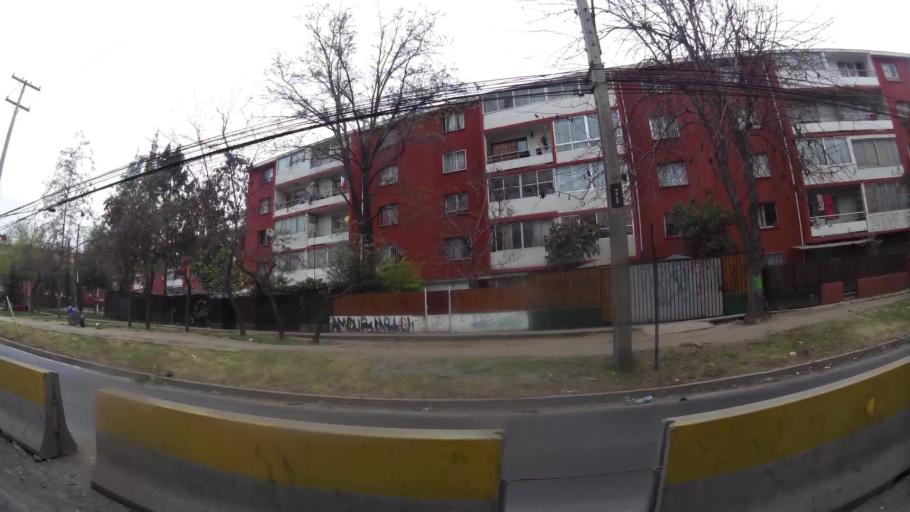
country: CL
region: Santiago Metropolitan
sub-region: Provincia de Santiago
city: Santiago
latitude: -33.4925
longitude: -70.6175
